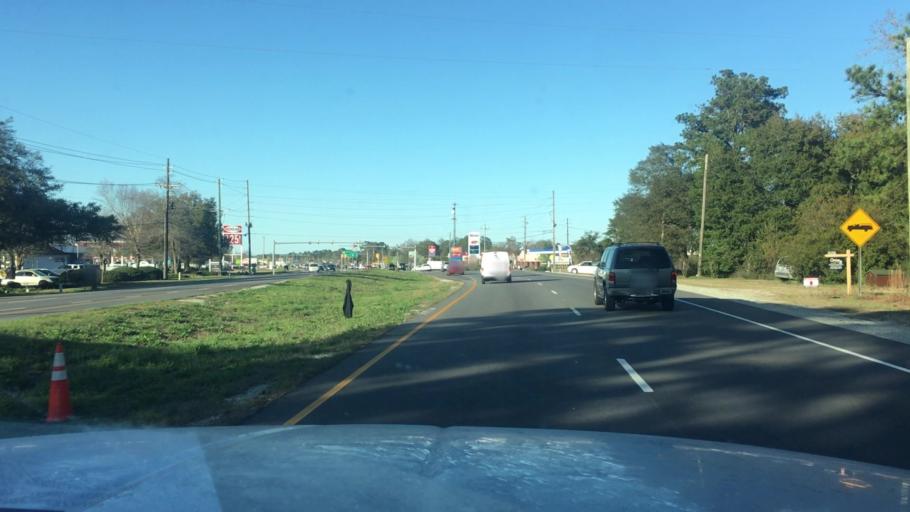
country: US
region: North Carolina
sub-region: New Hanover County
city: Myrtle Grove
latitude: 34.1326
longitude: -77.8956
